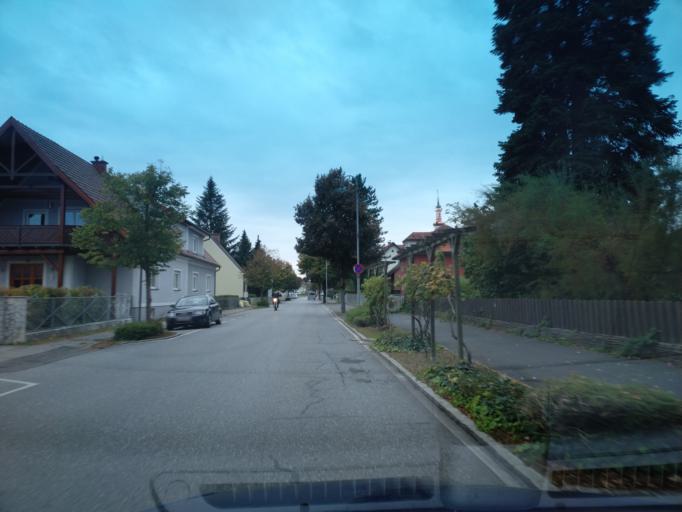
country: AT
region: Styria
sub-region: Politischer Bezirk Leibnitz
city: Leibnitz
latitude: 46.7858
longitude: 15.5412
